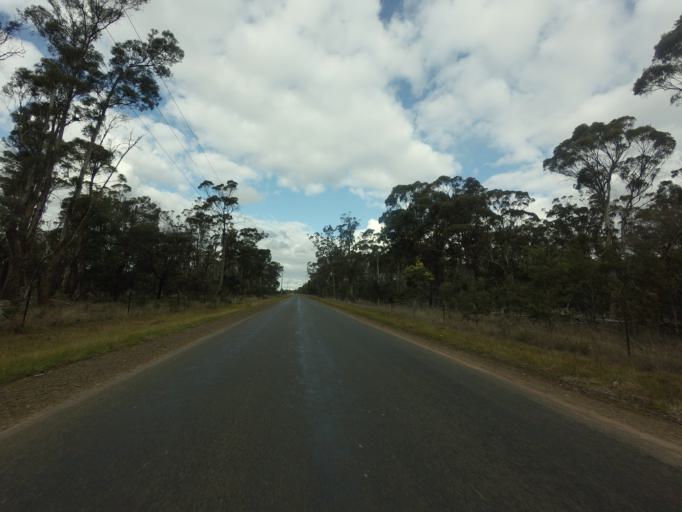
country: AU
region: Tasmania
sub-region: Northern Midlands
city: Longford
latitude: -41.7969
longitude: 147.1229
